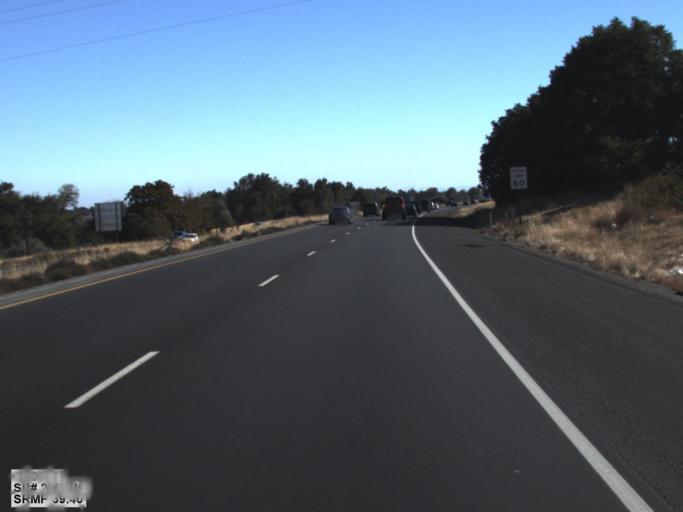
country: US
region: Washington
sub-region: Franklin County
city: West Pasco
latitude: 46.2321
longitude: -119.2131
